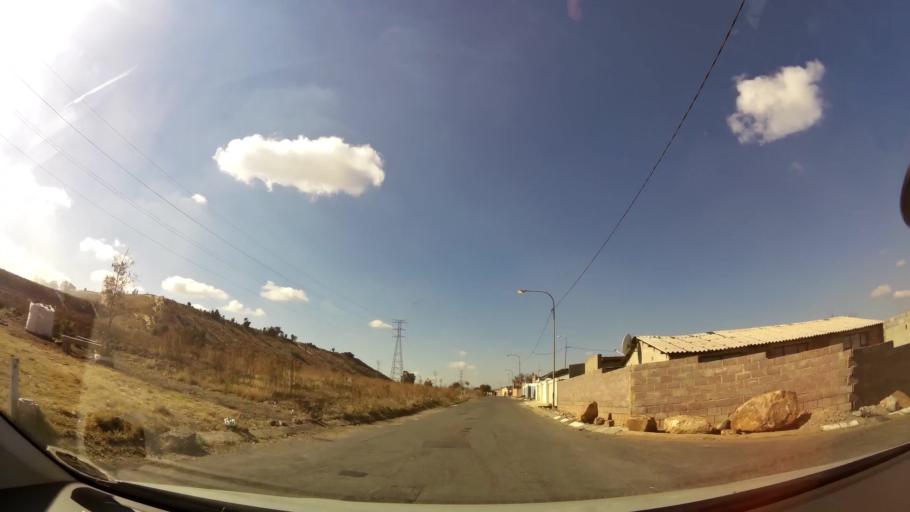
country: ZA
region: Gauteng
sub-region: City of Johannesburg Metropolitan Municipality
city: Roodepoort
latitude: -26.2044
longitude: 27.8861
